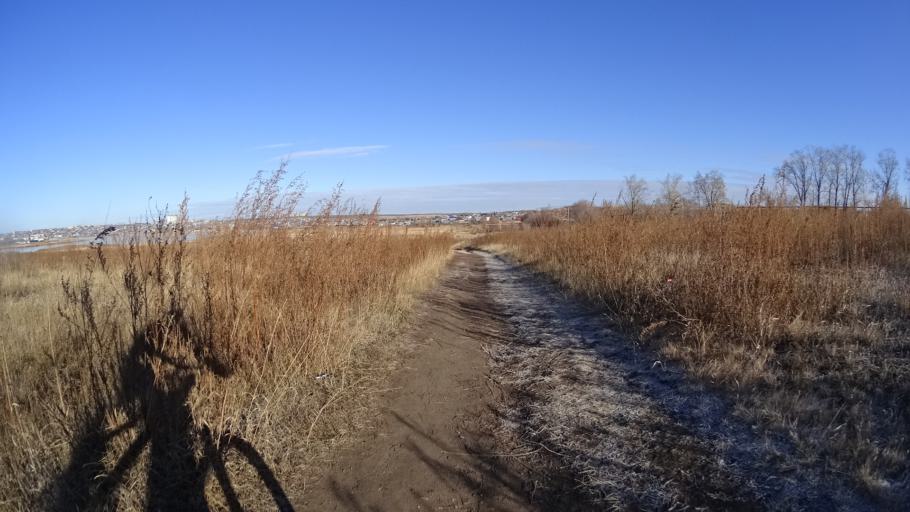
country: RU
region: Chelyabinsk
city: Troitsk
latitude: 54.0801
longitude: 61.5902
